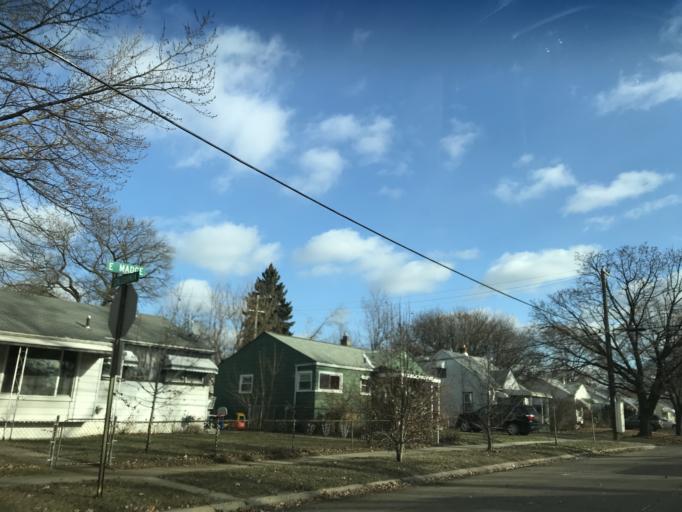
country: US
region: Michigan
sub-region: Oakland County
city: Hazel Park
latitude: 42.4538
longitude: -83.0977
